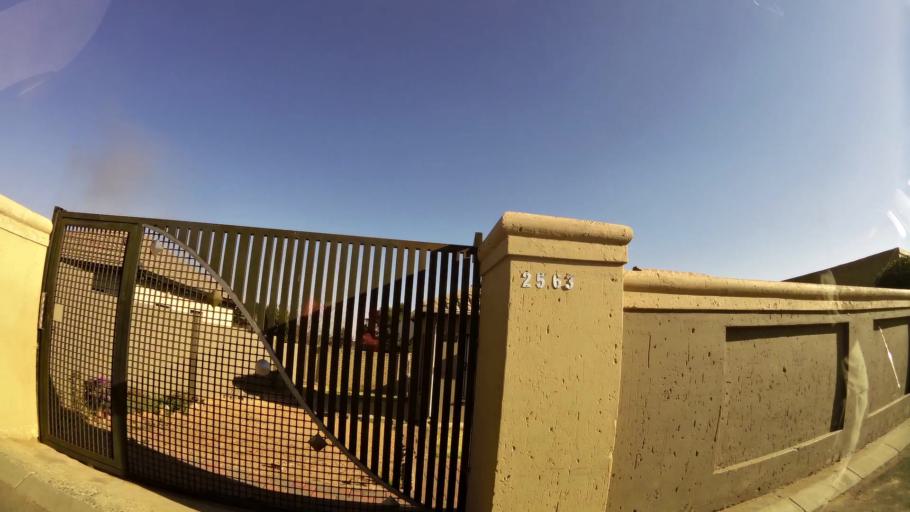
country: ZA
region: Gauteng
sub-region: City of Johannesburg Metropolitan Municipality
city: Johannesburg
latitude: -26.2101
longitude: 27.9704
